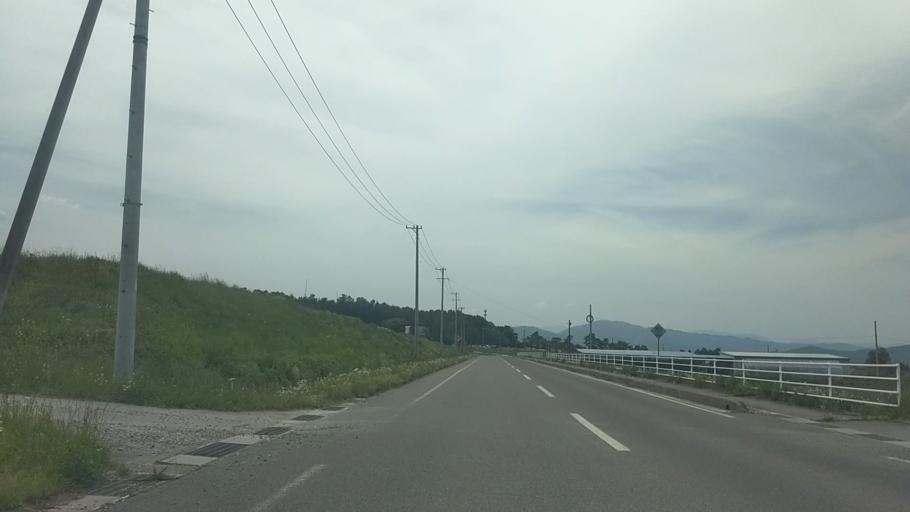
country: JP
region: Nagano
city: Chino
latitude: 36.0271
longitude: 138.2353
